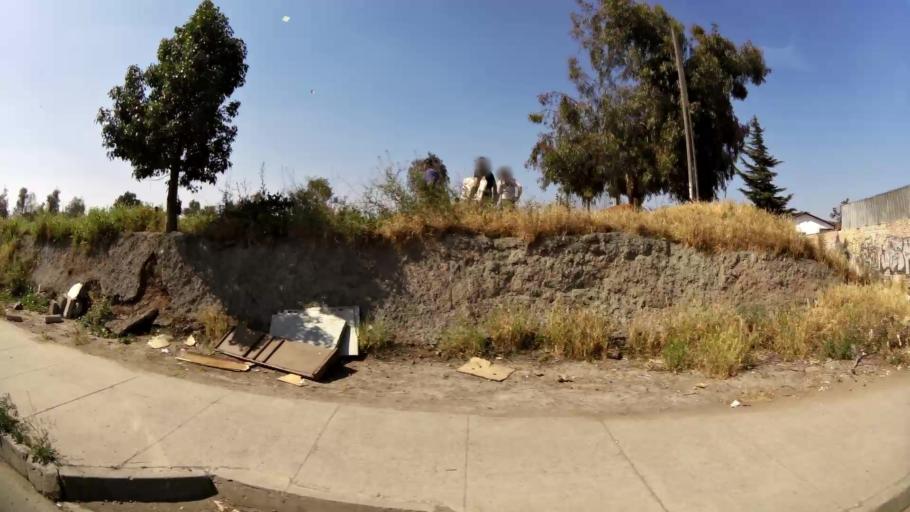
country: CL
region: Santiago Metropolitan
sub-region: Provincia de Santiago
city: Lo Prado
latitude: -33.4050
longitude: -70.6953
